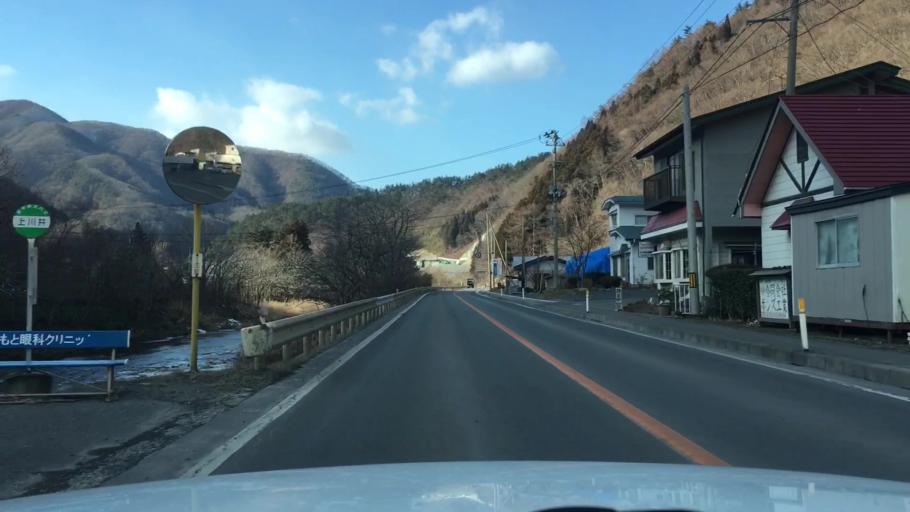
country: JP
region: Iwate
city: Miyako
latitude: 39.5934
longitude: 141.6630
